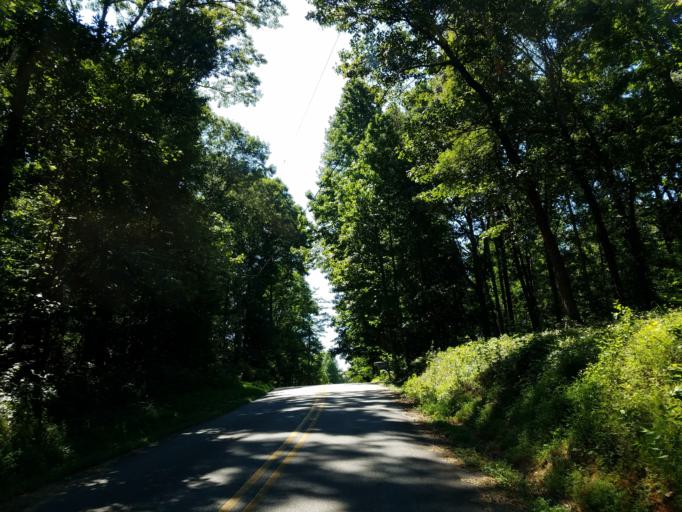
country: US
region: Georgia
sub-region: Lumpkin County
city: Dahlonega
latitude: 34.4150
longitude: -83.9988
